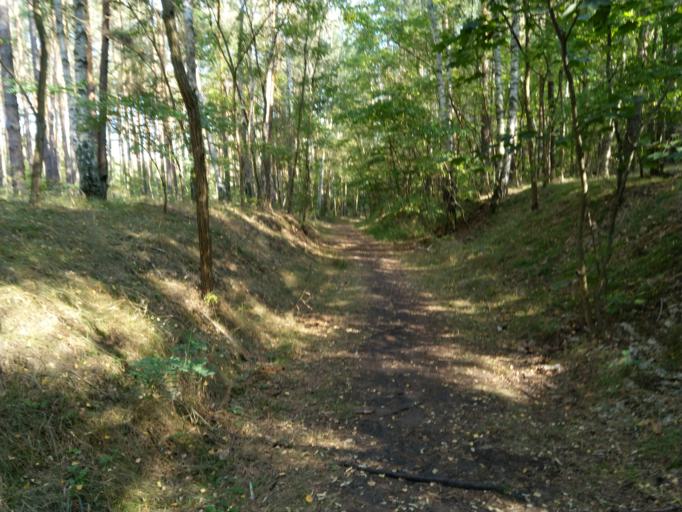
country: DE
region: Brandenburg
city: Erkner
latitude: 52.4441
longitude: 13.7303
